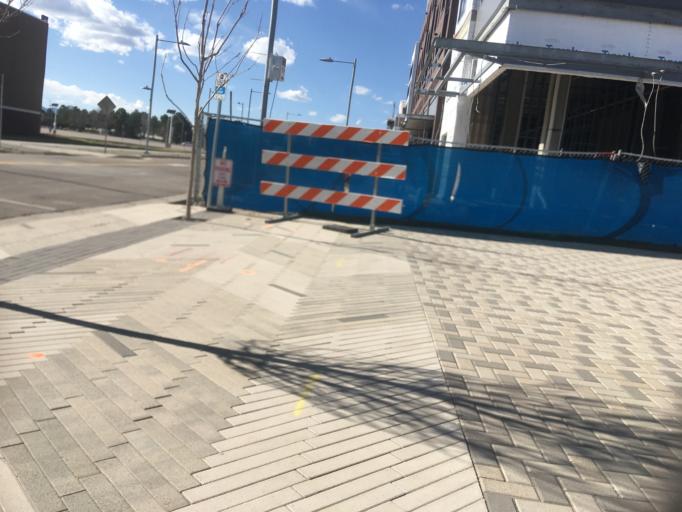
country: US
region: Colorado
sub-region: Adams County
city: Westminster
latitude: 39.8587
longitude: -105.0614
